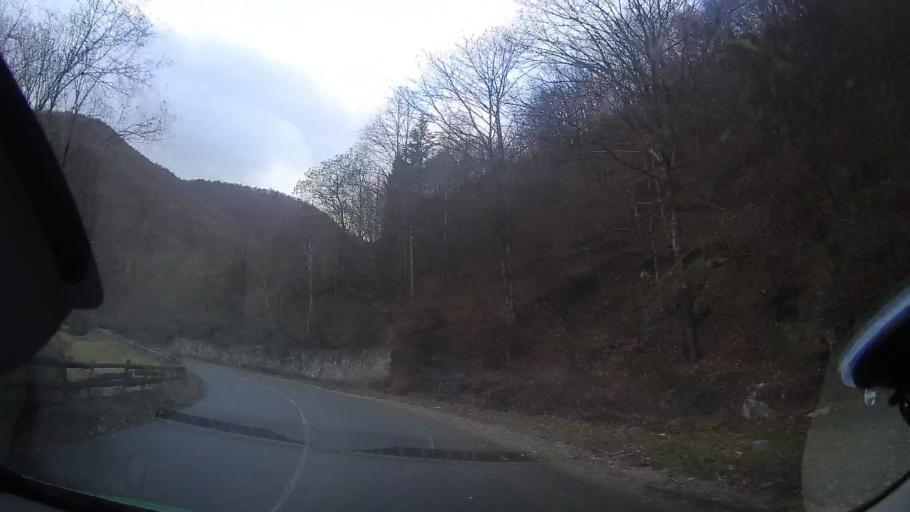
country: RO
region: Cluj
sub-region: Comuna Maguri-Racatau
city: Maguri-Racatau
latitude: 46.6673
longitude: 23.2428
